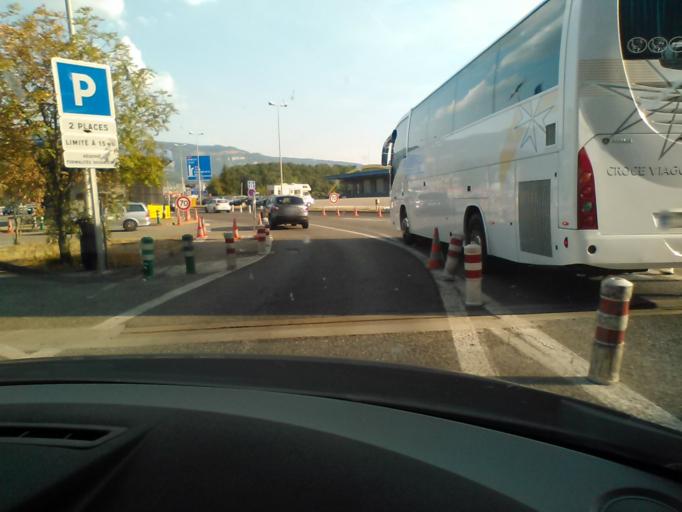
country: FR
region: Rhone-Alpes
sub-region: Departement de la Haute-Savoie
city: Saint-Julien-en-Genevois
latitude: 46.1466
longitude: 6.0955
